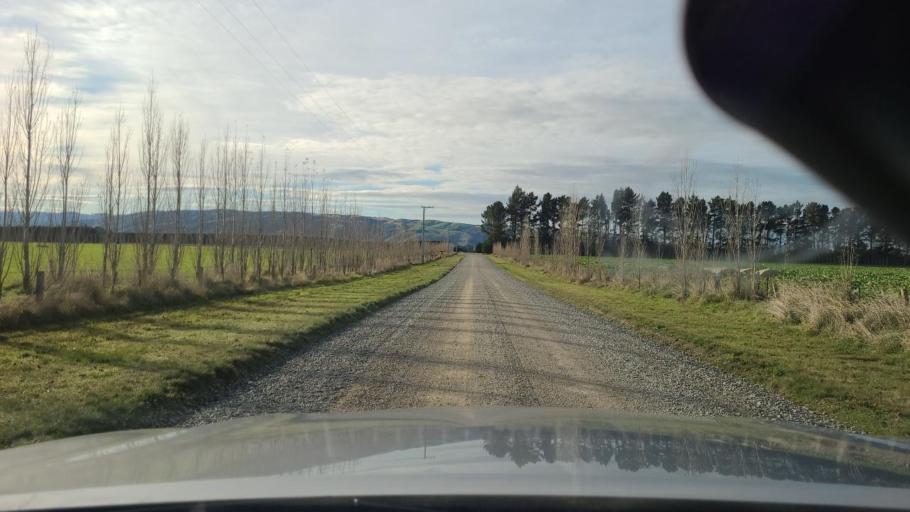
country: NZ
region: Southland
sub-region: Gore District
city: Gore
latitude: -45.7921
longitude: 168.7356
